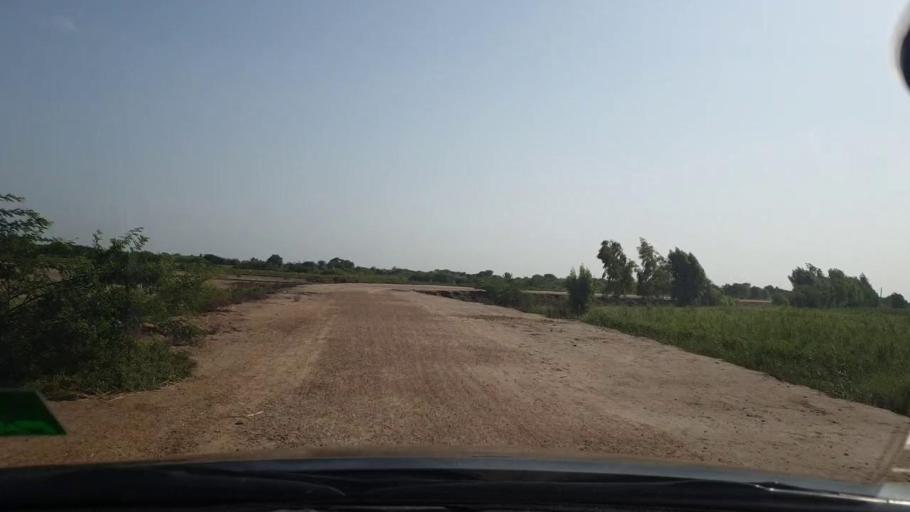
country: PK
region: Sindh
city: Tando Bago
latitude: 24.6974
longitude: 69.0152
